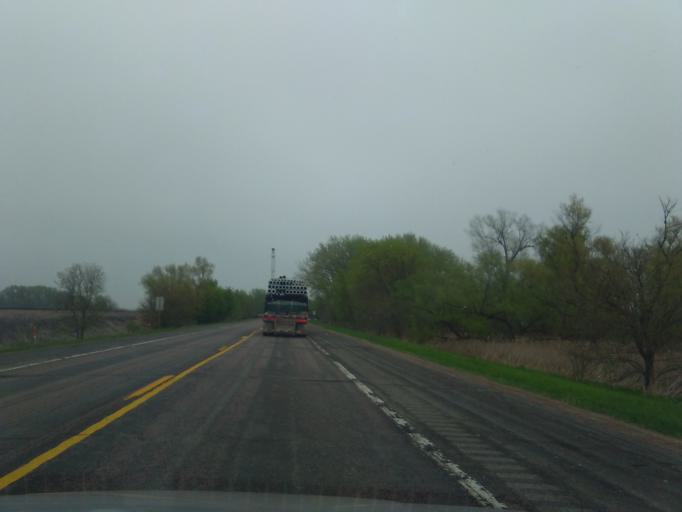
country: US
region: Nebraska
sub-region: Burt County
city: Oakland
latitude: 41.8067
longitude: -96.4785
